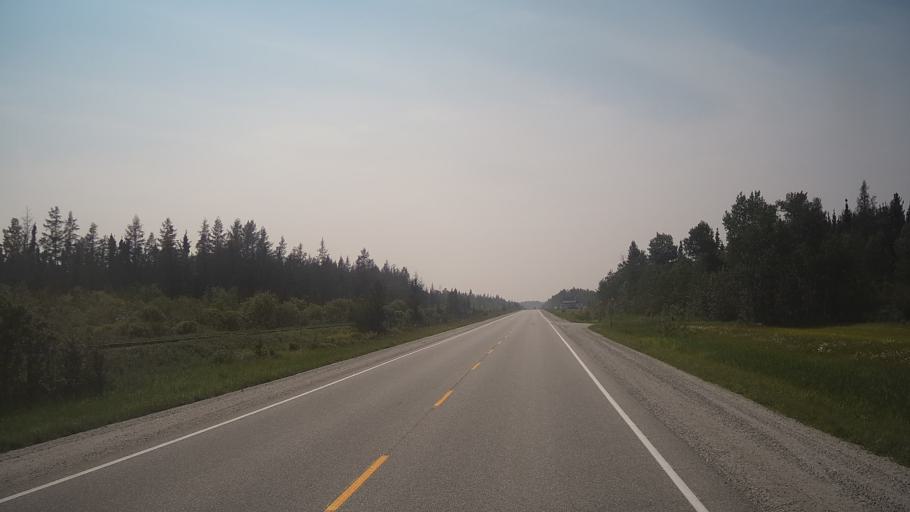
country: CA
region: Ontario
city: Kapuskasing
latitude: 49.2886
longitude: -81.9084
